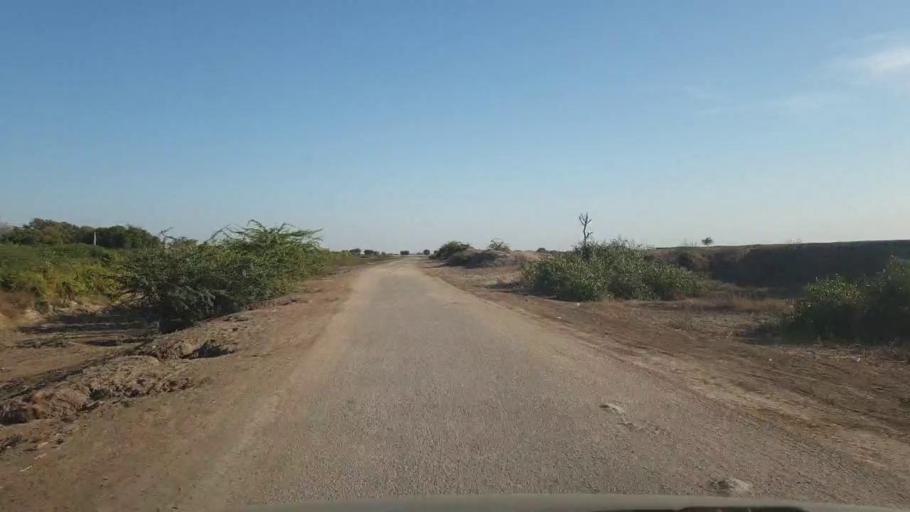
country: PK
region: Sindh
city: Dhoro Naro
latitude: 25.4276
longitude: 69.5330
